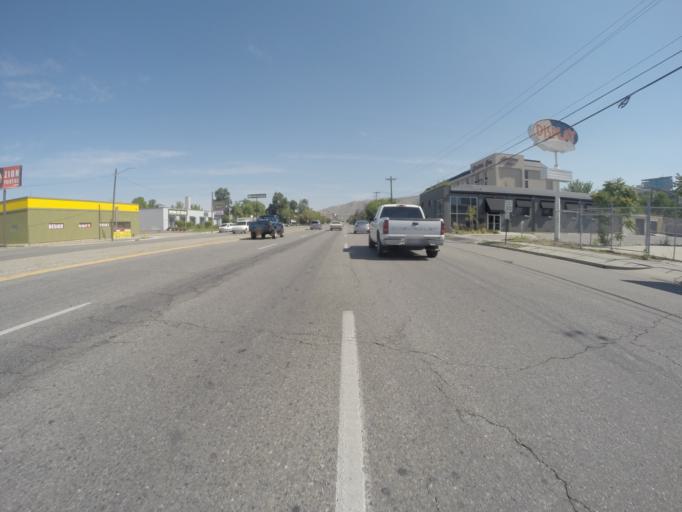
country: US
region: Utah
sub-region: Salt Lake County
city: Salt Lake City
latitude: 40.7588
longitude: -111.8996
